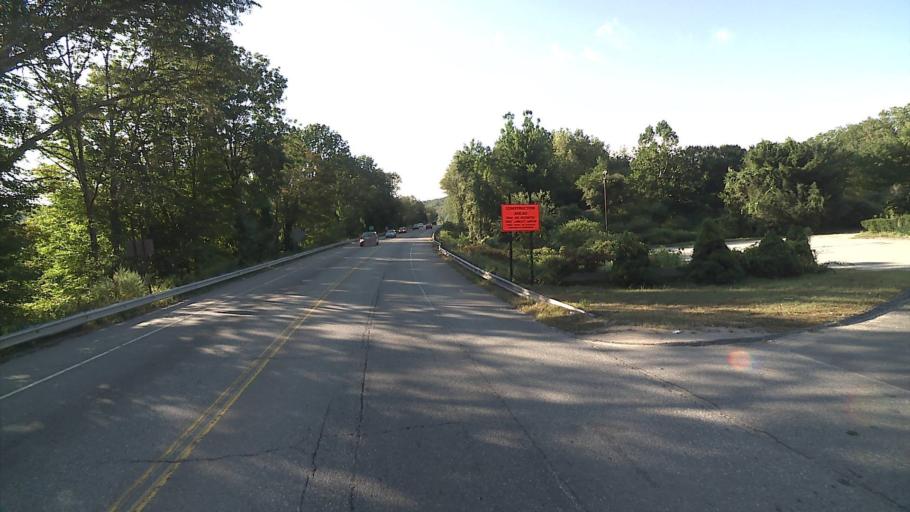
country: US
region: Connecticut
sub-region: New London County
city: Norwich
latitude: 41.5657
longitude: -72.1285
